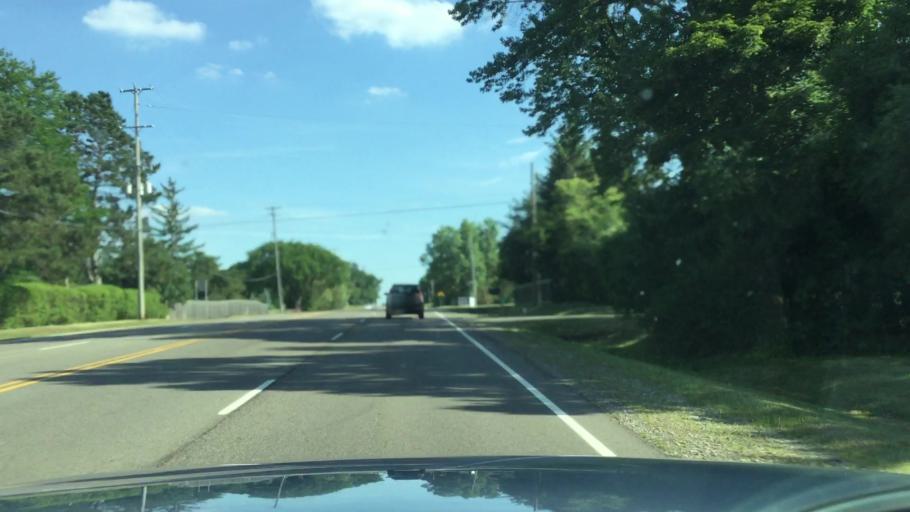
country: US
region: Michigan
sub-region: Genesee County
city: Grand Blanc
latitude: 42.9008
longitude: -83.6022
